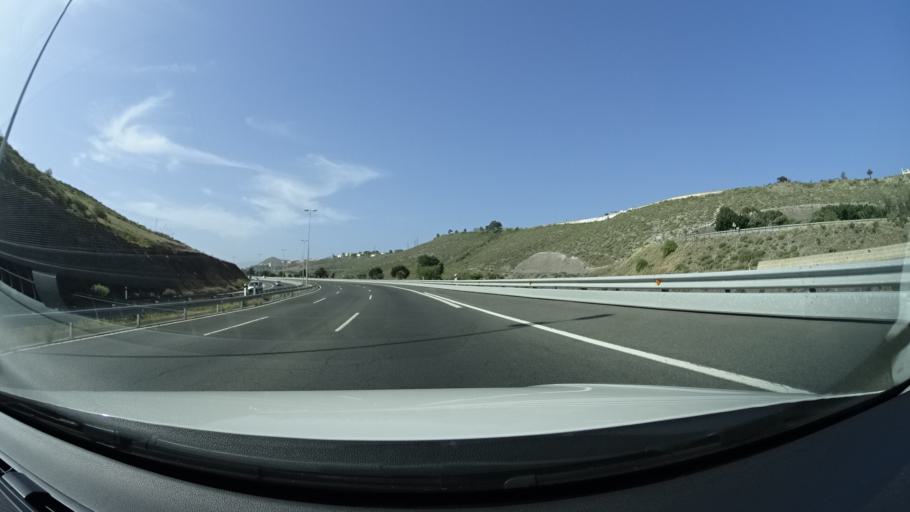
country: ES
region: Canary Islands
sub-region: Provincia de Las Palmas
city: Las Palmas de Gran Canaria
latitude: 28.0834
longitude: -15.4339
